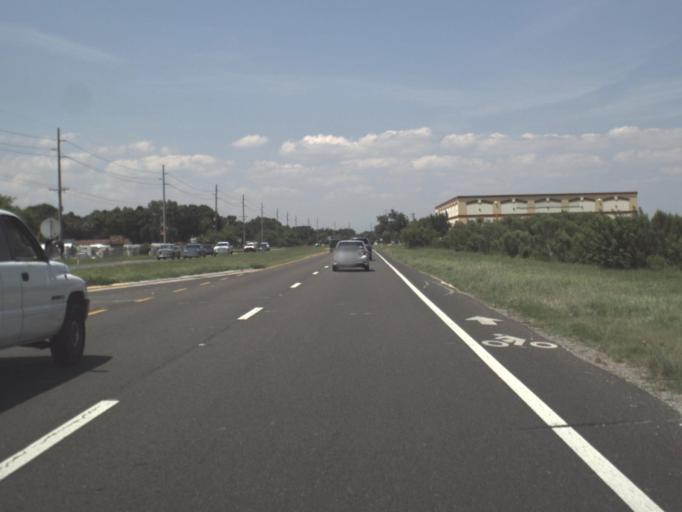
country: US
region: Florida
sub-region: Hillsborough County
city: Apollo Beach
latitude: 27.8080
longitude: -82.3841
